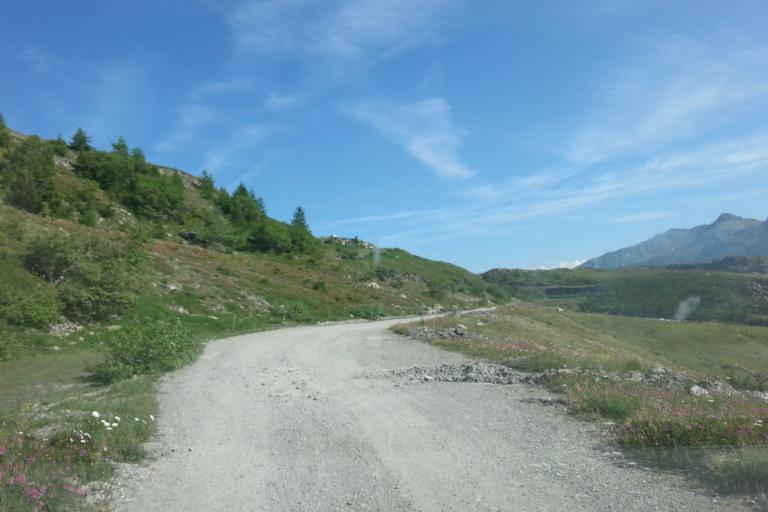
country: IT
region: Piedmont
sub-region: Provincia di Torino
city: Moncenisio
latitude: 45.2210
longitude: 6.9651
